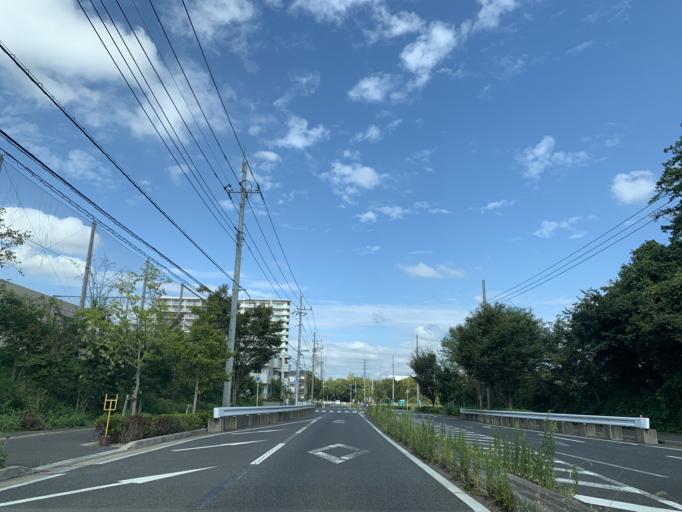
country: JP
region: Chiba
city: Nagareyama
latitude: 35.8545
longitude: 139.9167
